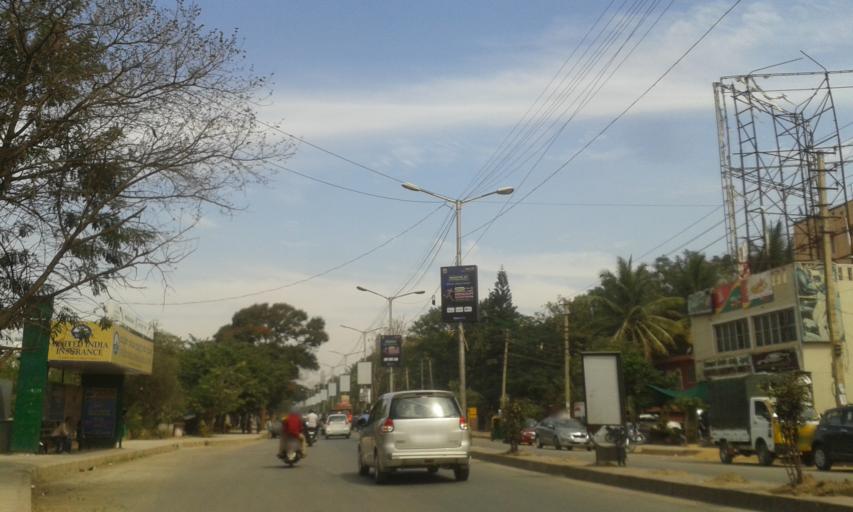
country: IN
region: Karnataka
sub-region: Bangalore Rural
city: Hoskote
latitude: 12.9766
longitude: 77.7509
